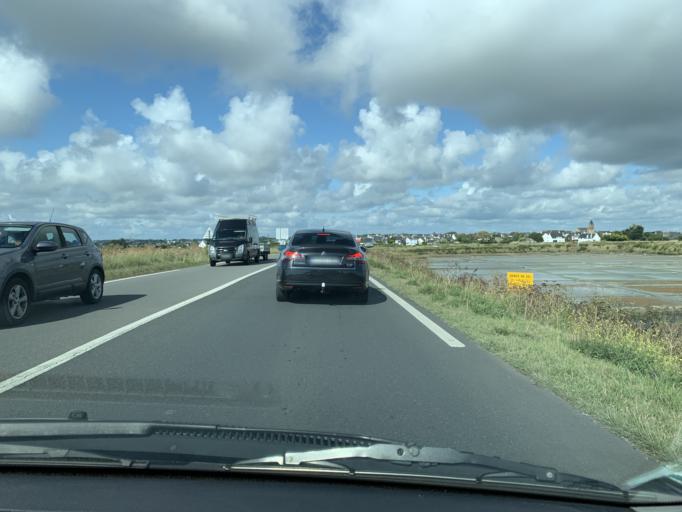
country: FR
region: Pays de la Loire
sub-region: Departement de la Loire-Atlantique
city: Le Pouliguen
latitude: 47.2913
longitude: -2.4383
